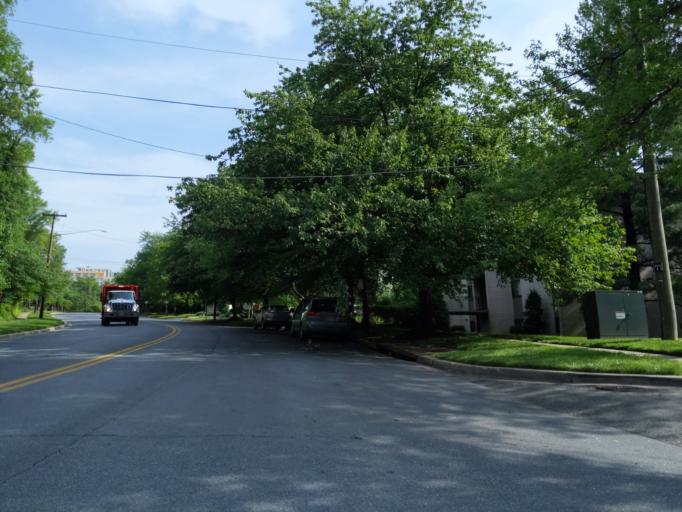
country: US
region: Maryland
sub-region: Montgomery County
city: Wheaton
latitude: 39.0330
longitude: -77.0470
